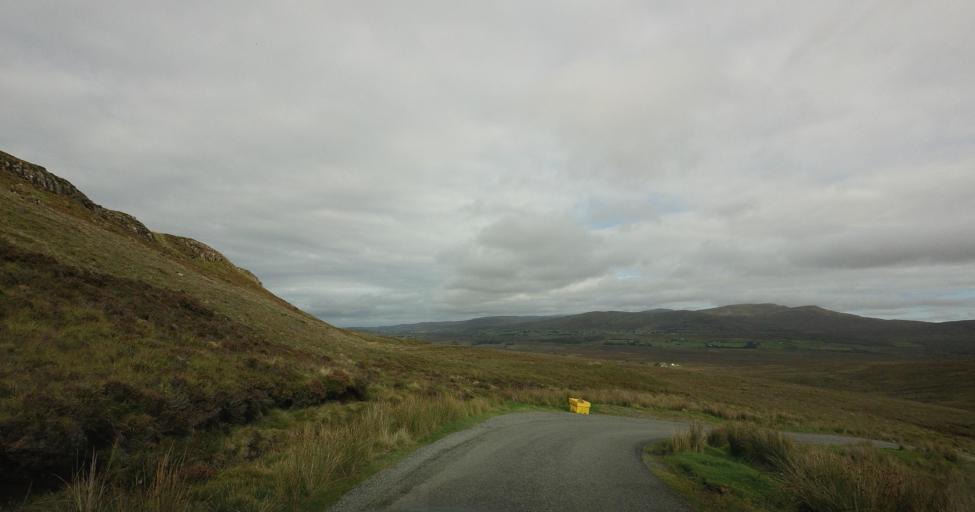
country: GB
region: Scotland
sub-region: Highland
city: Isle of Skye
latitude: 57.4127
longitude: -6.2604
